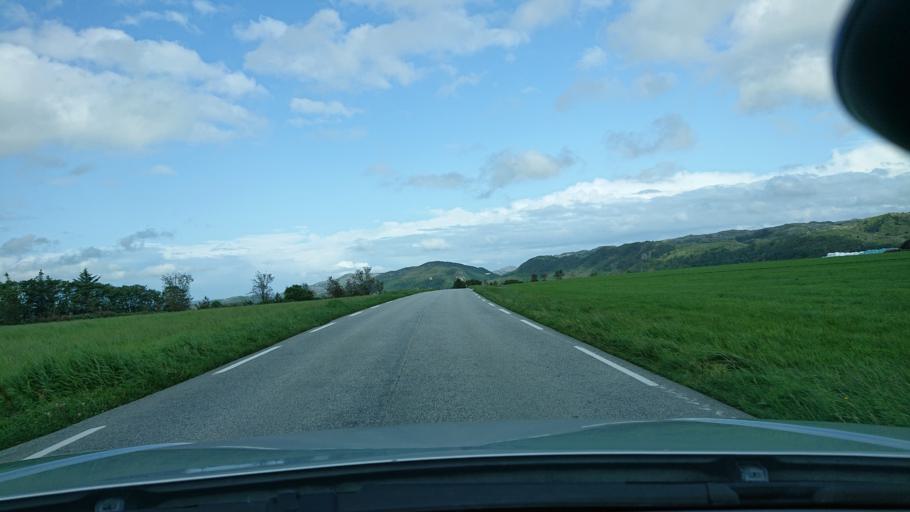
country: NO
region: Rogaland
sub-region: Gjesdal
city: Algard
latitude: 58.6926
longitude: 5.7723
